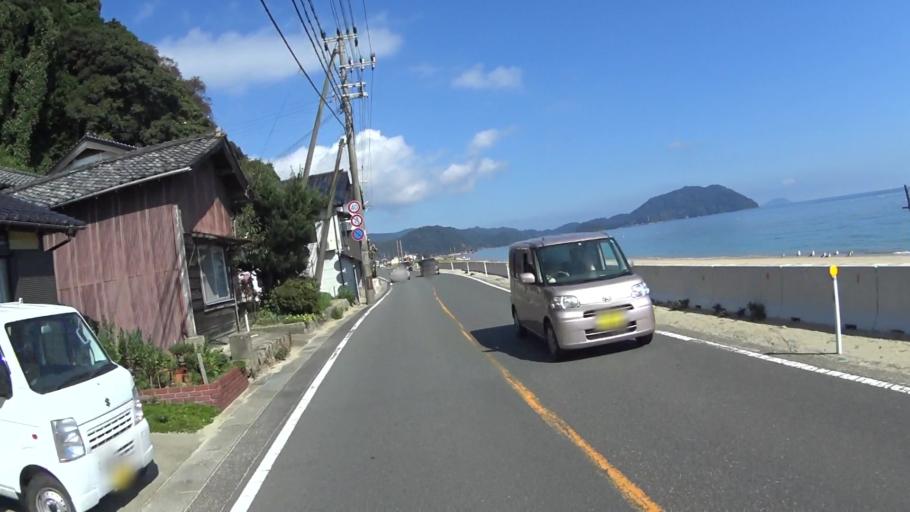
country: JP
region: Kyoto
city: Miyazu
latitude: 35.6508
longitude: 135.2541
